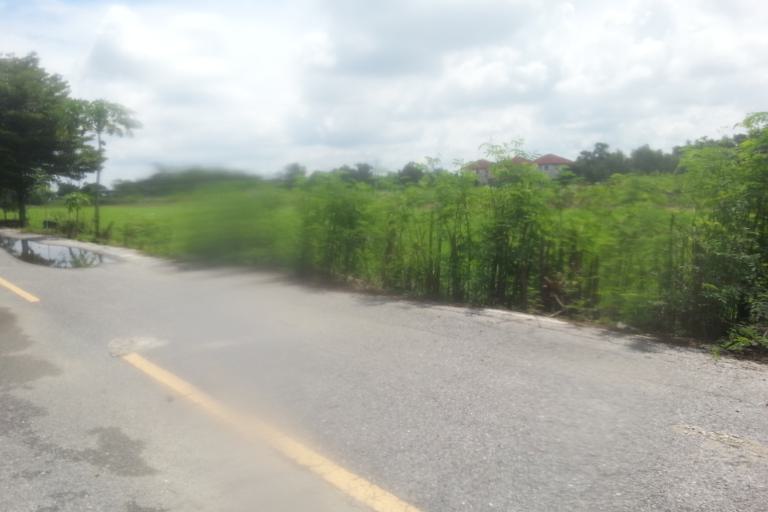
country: TH
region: Pathum Thani
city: Nong Suea
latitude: 14.0613
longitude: 100.8589
